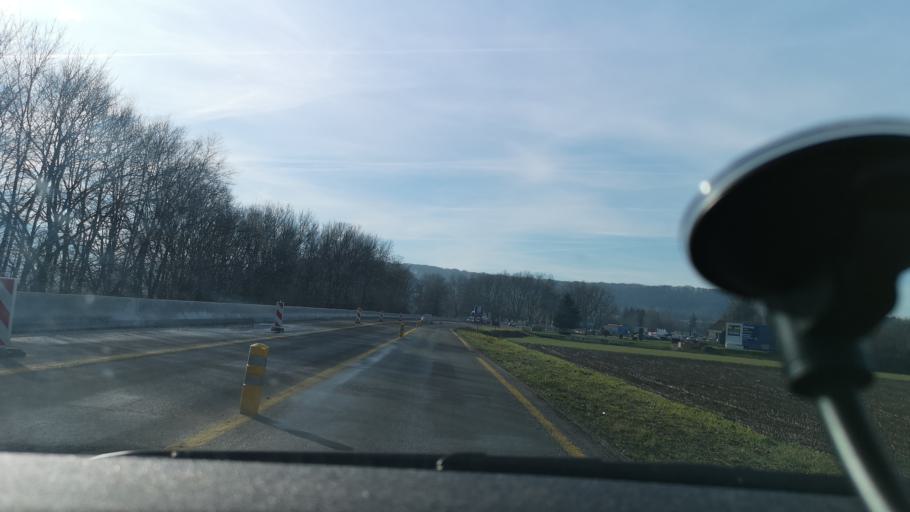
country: FR
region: Franche-Comte
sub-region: Departement du Doubs
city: Thise
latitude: 47.2688
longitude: 6.0764
